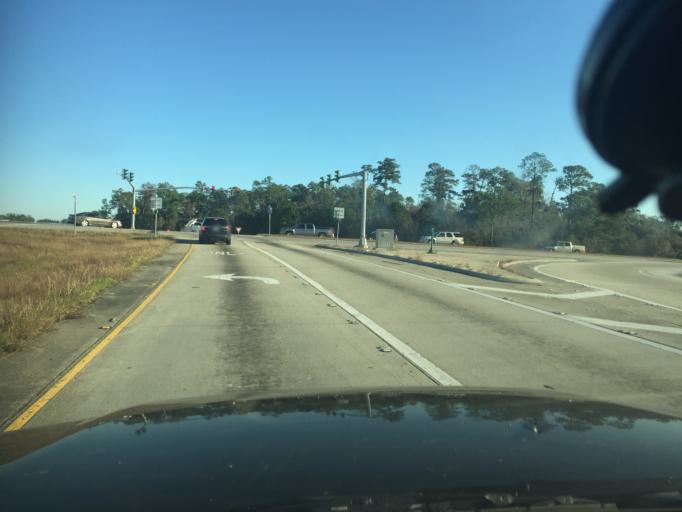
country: US
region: Louisiana
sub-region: Saint Tammany Parish
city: Slidell
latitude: 30.2694
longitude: -89.7543
